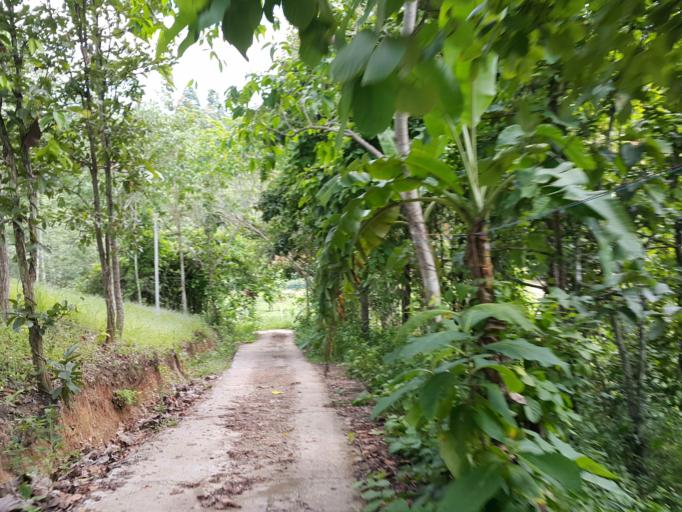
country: TH
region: Chiang Mai
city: Mae Taeng
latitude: 18.9560
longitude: 98.9134
